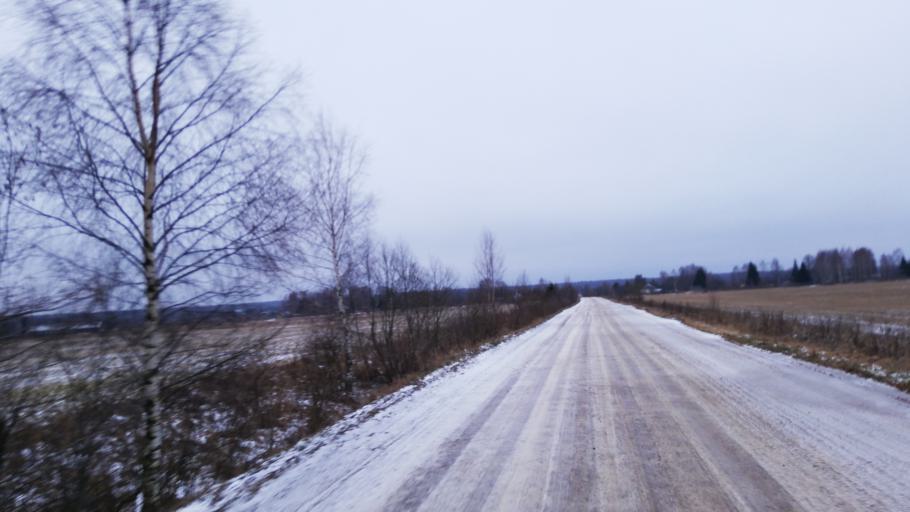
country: RU
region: Kostroma
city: Krasnoye-na-Volge
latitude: 57.6761
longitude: 41.1959
